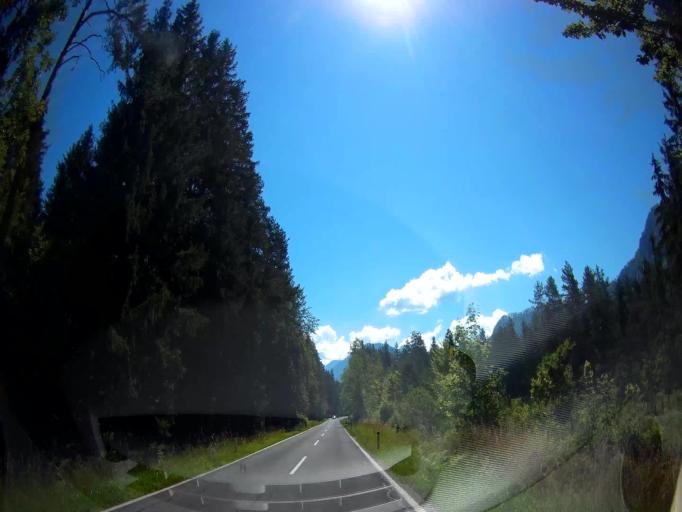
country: AT
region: Carinthia
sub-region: Politischer Bezirk Volkermarkt
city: Gallizien
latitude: 46.5421
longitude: 14.5479
